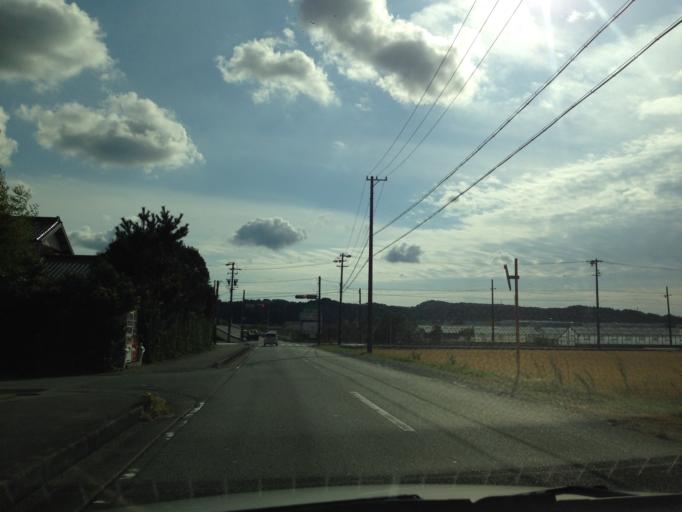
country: JP
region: Shizuoka
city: Fukuroi
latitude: 34.7562
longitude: 137.9522
